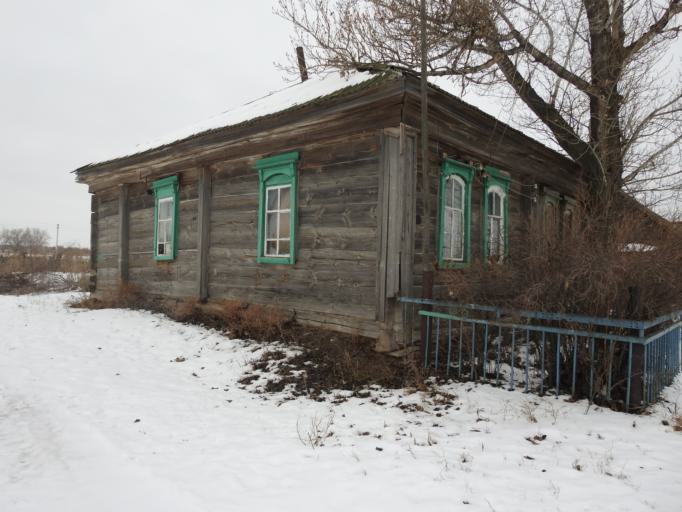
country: RU
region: Saratov
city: Sovetskoye
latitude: 51.5374
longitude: 46.5966
